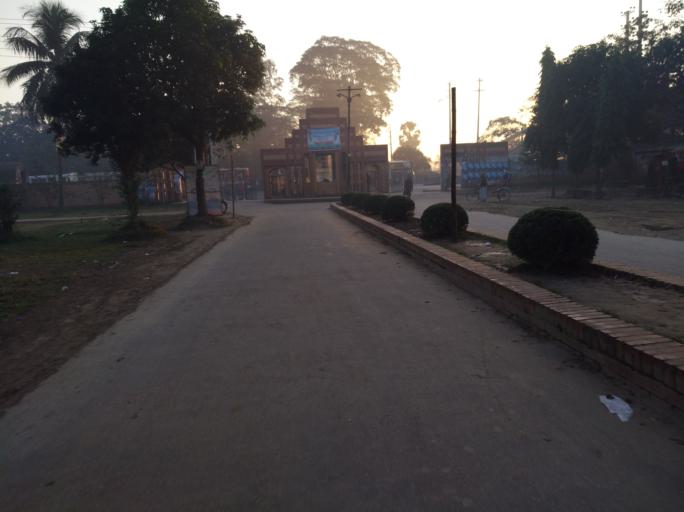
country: BD
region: Dhaka
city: Tungi
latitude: 23.8799
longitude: 90.2723
